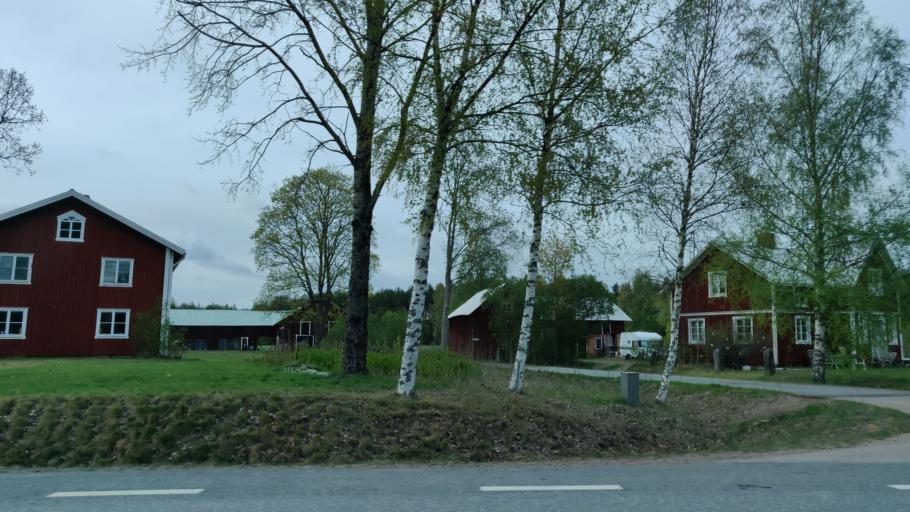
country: SE
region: Vaermland
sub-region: Munkfors Kommun
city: Munkfors
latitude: 59.7871
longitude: 13.4889
